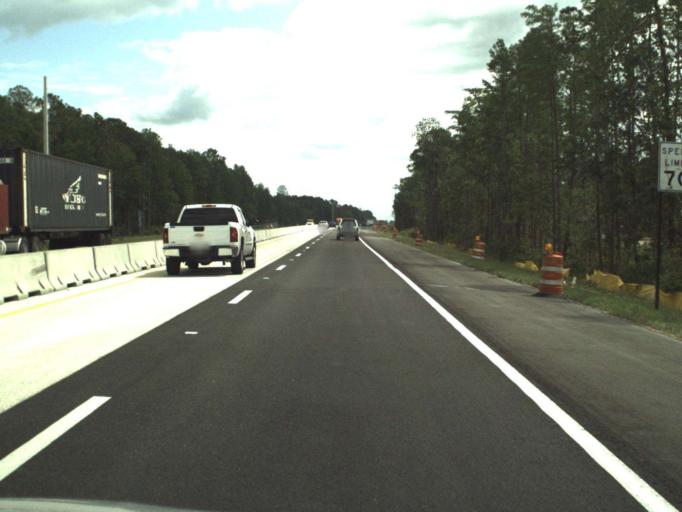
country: US
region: Florida
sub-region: Volusia County
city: Lake Helen
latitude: 29.0349
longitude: -81.2156
